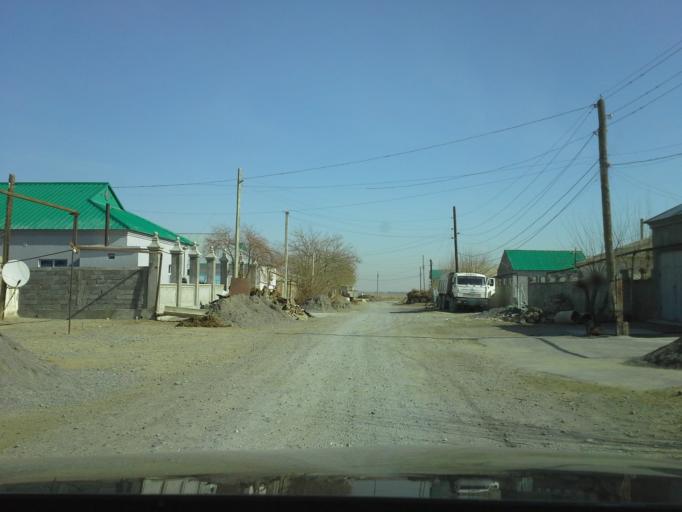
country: TM
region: Ahal
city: Arcabil
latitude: 38.1076
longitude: 57.9819
